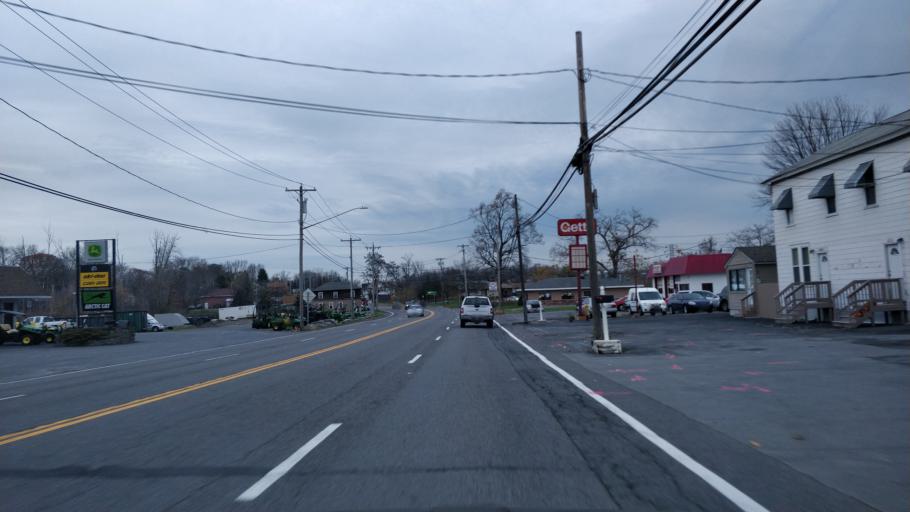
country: US
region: New York
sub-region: Onondaga County
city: North Syracuse
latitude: 43.1709
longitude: -76.1171
